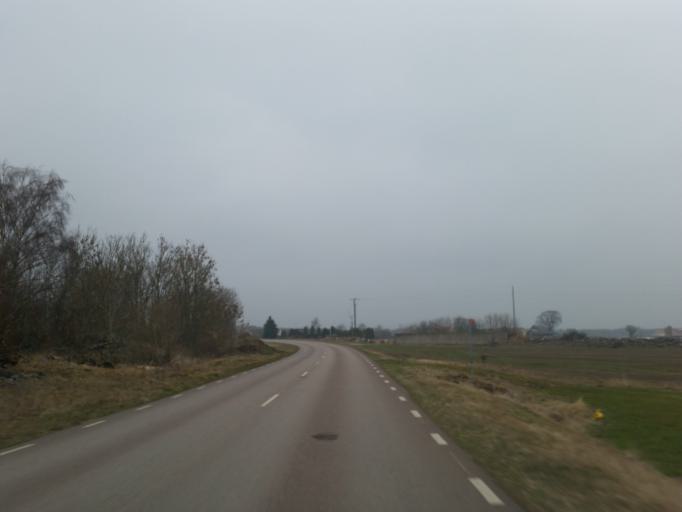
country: SE
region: Kalmar
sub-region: Morbylanga Kommun
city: Sodra Sandby
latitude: 56.6101
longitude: 16.6189
